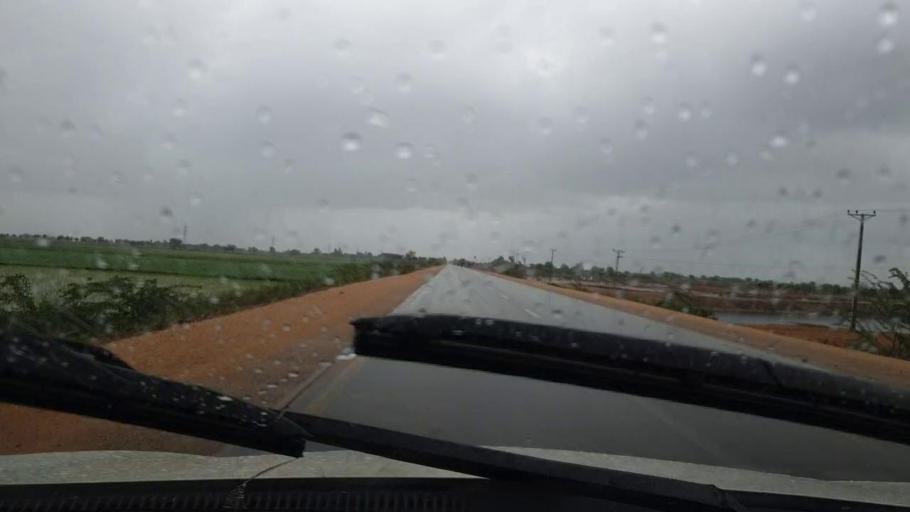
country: PK
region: Sindh
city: Kario
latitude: 24.6532
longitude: 68.5902
